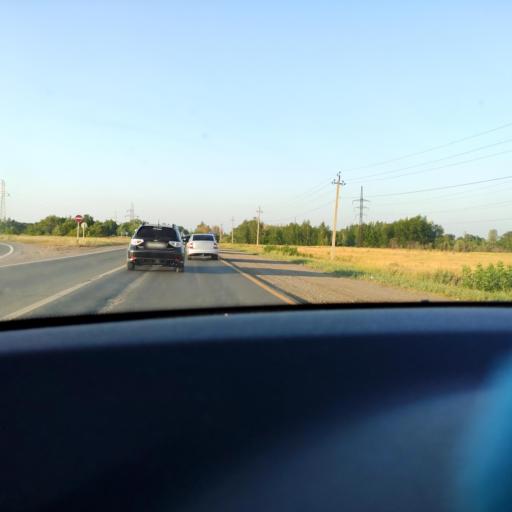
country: RU
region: Samara
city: Kinel'
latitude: 53.2468
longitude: 50.5881
